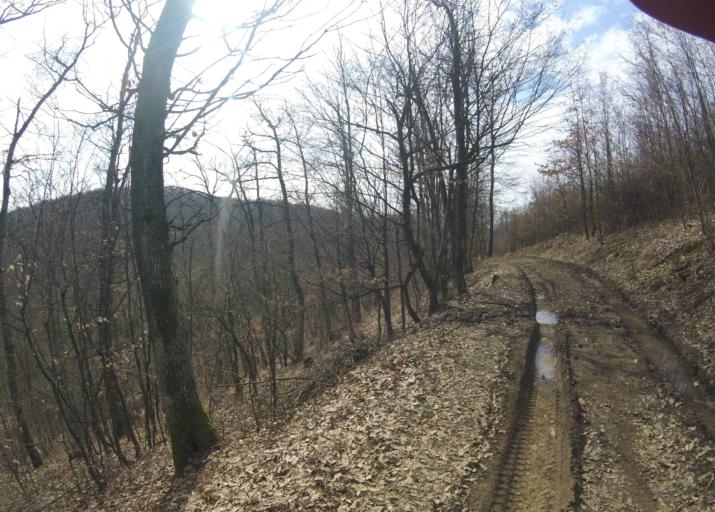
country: HU
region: Heves
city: Belapatfalva
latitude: 48.0166
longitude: 20.3484
